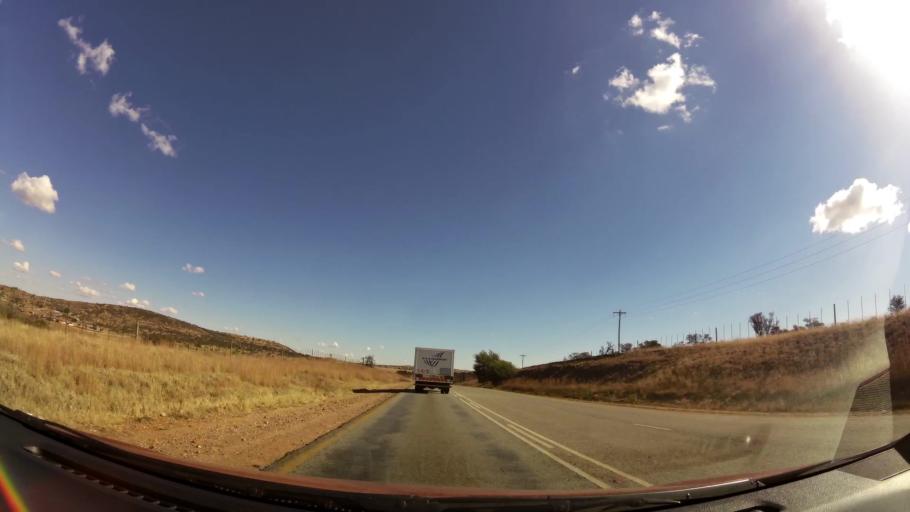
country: ZA
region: North-West
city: Fochville
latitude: -26.4372
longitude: 27.5020
